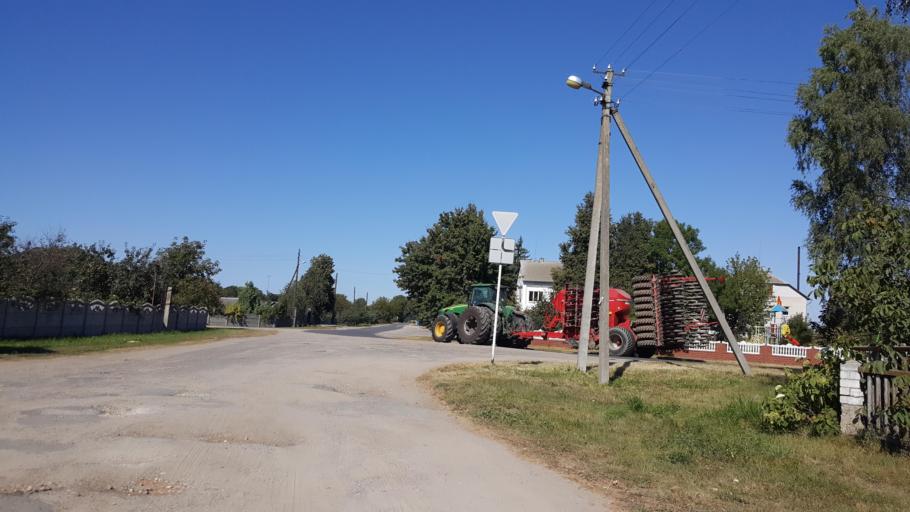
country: BY
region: Brest
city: Vysokaye
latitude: 52.2588
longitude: 23.4980
